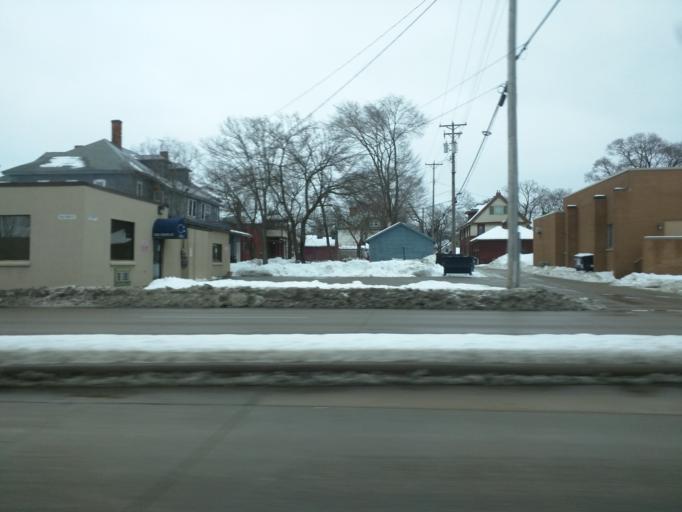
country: US
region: Wisconsin
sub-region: La Crosse County
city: La Crosse
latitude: 43.8123
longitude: -91.2389
